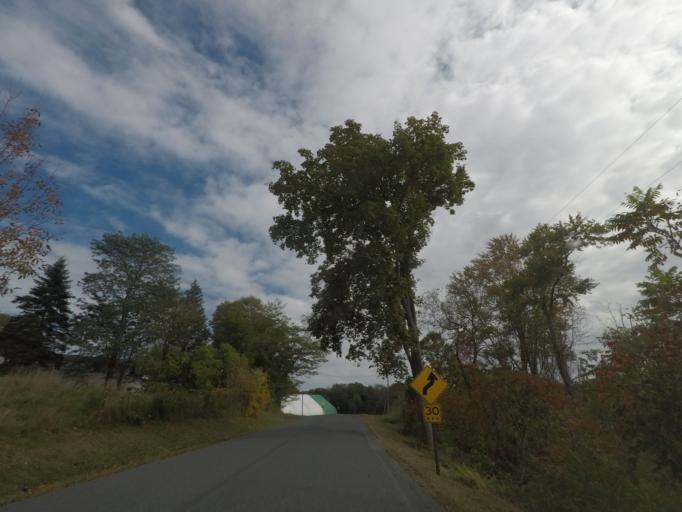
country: US
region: New York
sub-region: Rensselaer County
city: Nassau
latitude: 42.5437
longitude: -73.6264
